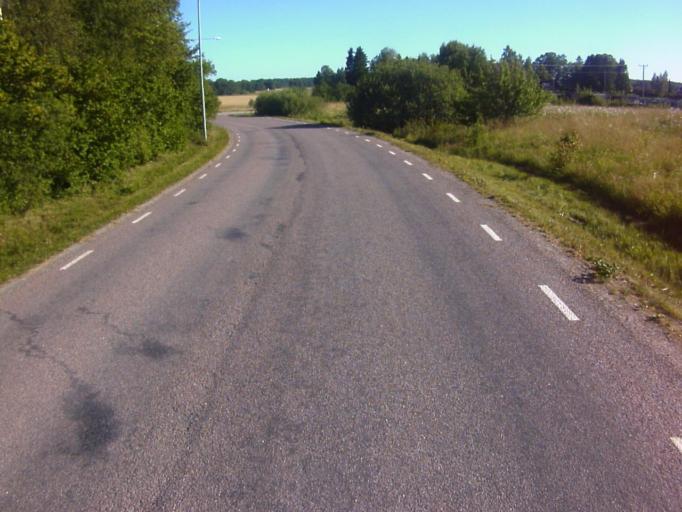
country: SE
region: Soedermanland
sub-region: Eskilstuna Kommun
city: Hallbybrunn
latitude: 59.3874
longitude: 16.4168
